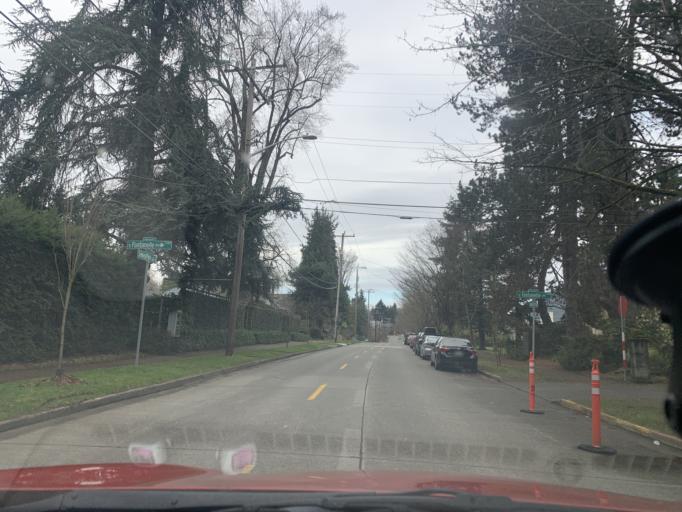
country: US
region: Washington
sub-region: King County
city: Bryn Mawr-Skyway
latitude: 47.5353
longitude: -122.2673
